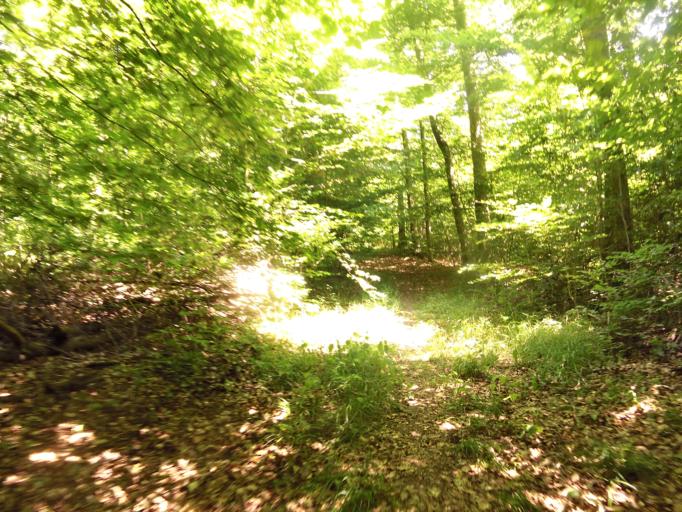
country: DE
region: Bavaria
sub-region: Regierungsbezirk Unterfranken
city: Gadheim
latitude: 49.8230
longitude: 9.9095
